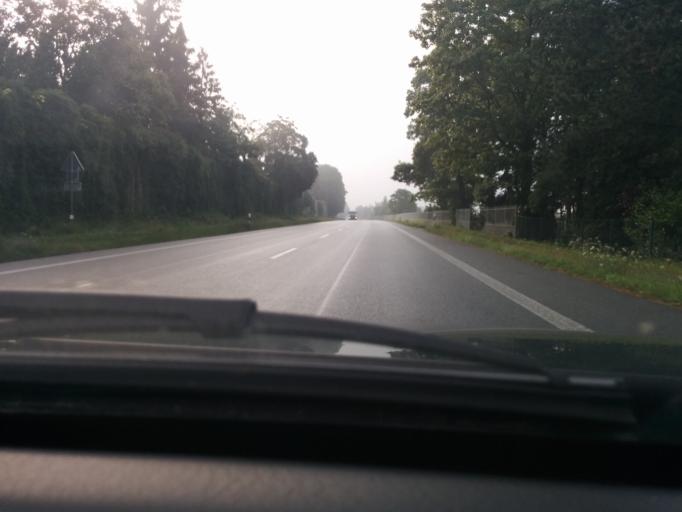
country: DE
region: North Rhine-Westphalia
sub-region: Regierungsbezirk Detmold
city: Steinhagen
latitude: 52.0212
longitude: 8.4277
